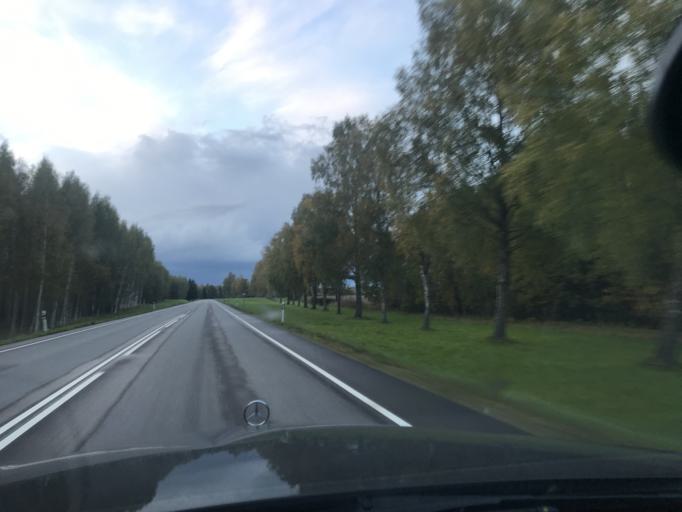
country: EE
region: Valgamaa
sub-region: Torva linn
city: Torva
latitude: 57.9807
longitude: 25.9481
